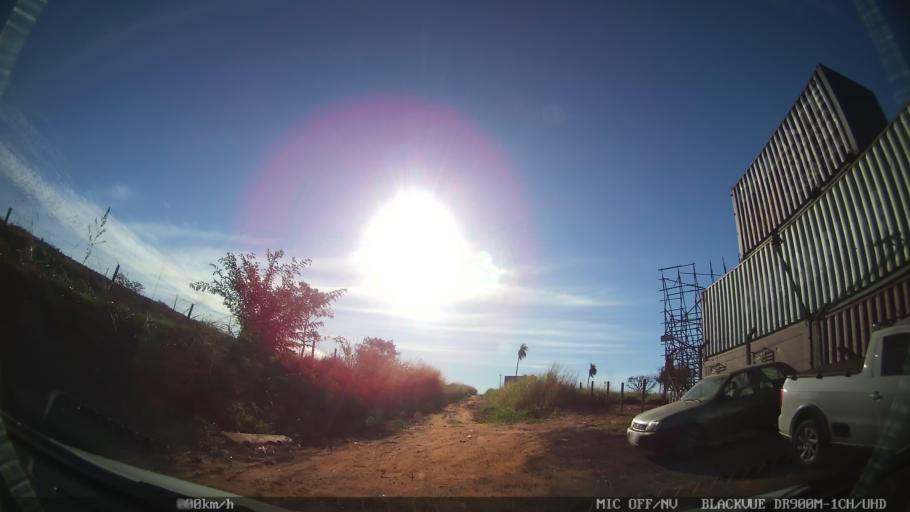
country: BR
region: Sao Paulo
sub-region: Sao Jose Do Rio Preto
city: Sao Jose do Rio Preto
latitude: -20.8815
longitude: -49.3157
